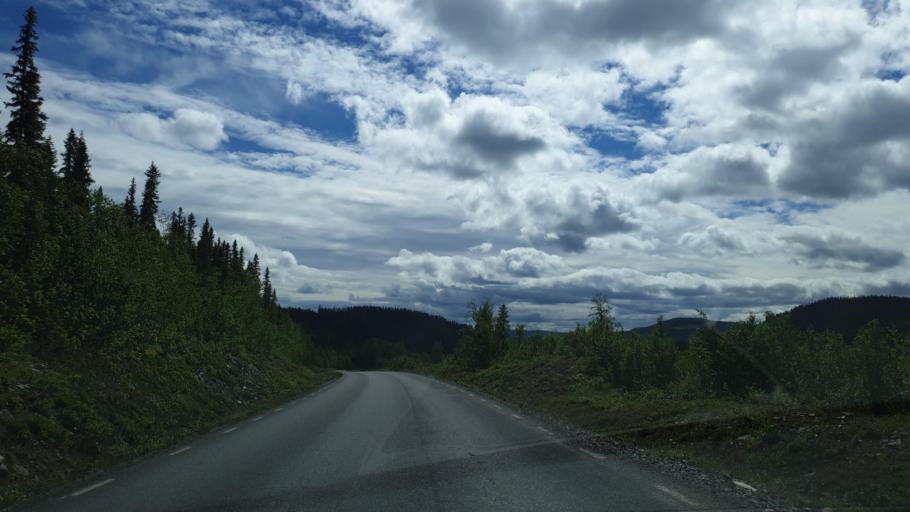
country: SE
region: Vaesterbotten
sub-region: Vilhelmina Kommun
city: Sjoberg
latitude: 64.9717
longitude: 15.8565
